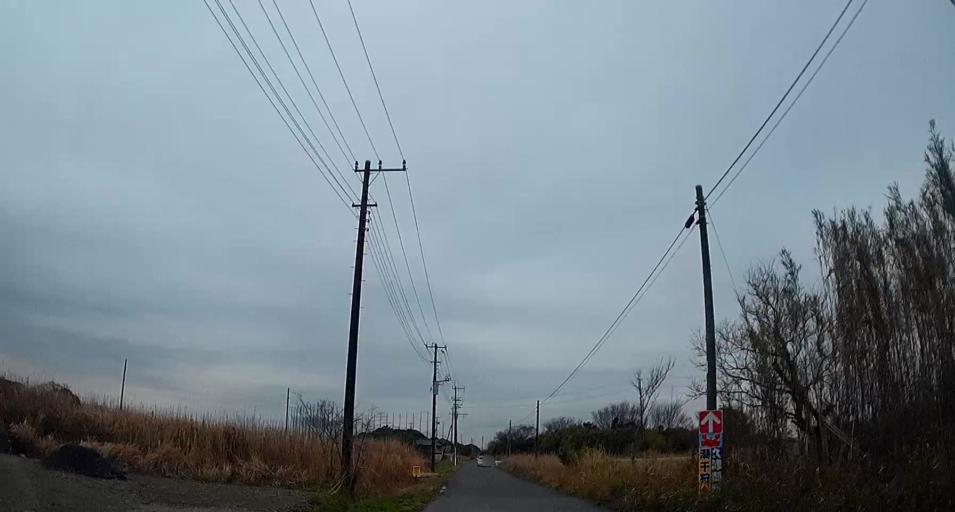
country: JP
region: Chiba
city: Kisarazu
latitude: 35.4111
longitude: 139.9053
